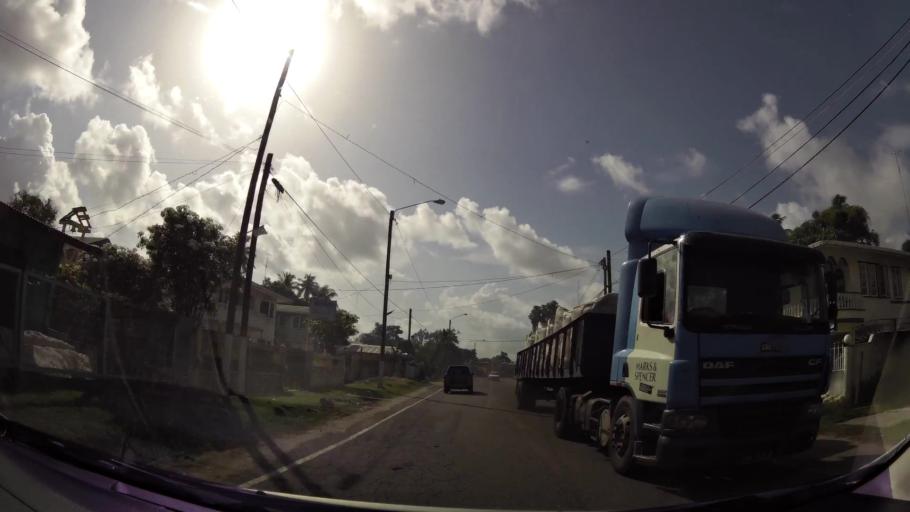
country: GY
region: Demerara-Mahaica
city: Mahaica Village
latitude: 6.7499
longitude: -57.9685
